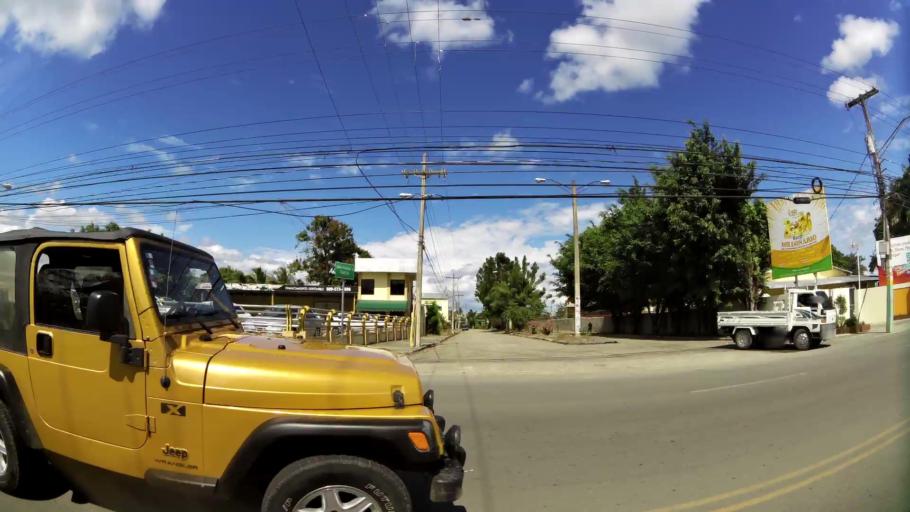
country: DO
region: La Vega
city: Concepcion de La Vega
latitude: 19.2339
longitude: -70.5308
